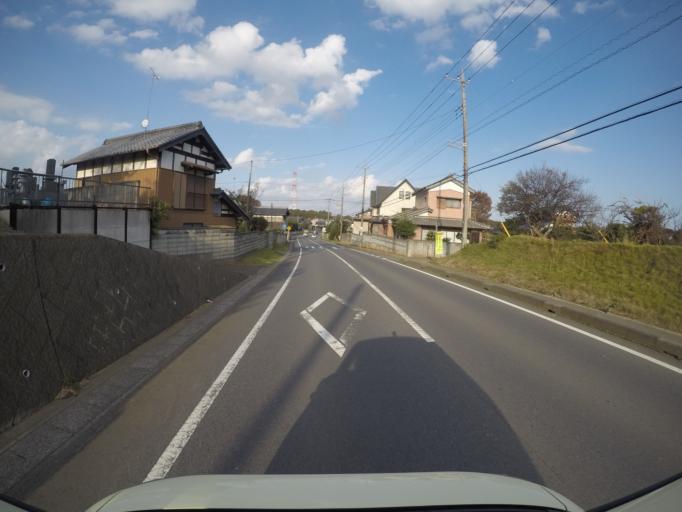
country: JP
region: Ibaraki
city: Ushiku
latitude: 36.0173
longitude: 140.0692
